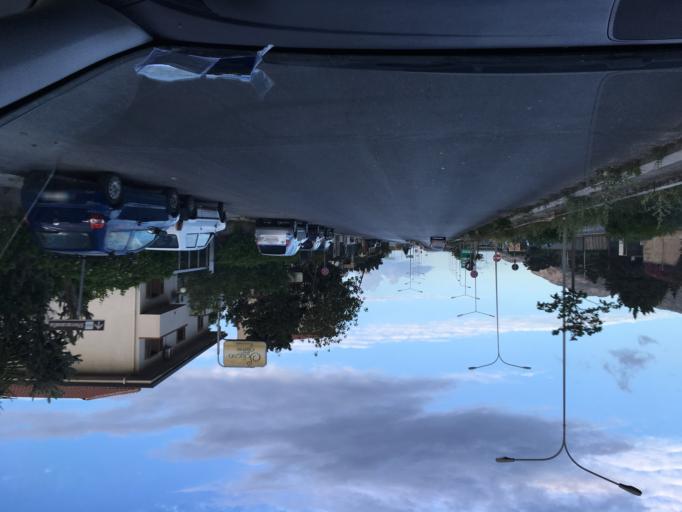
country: IT
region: Sicily
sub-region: Palermo
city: Isola delle Femmine
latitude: 38.1913
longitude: 13.2906
